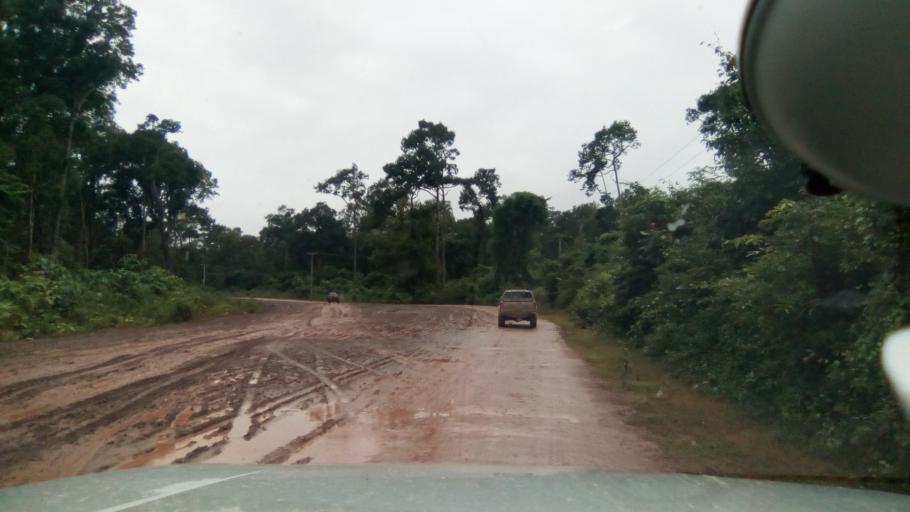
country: LA
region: Attapu
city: Attapu
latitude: 14.6830
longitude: 106.5558
